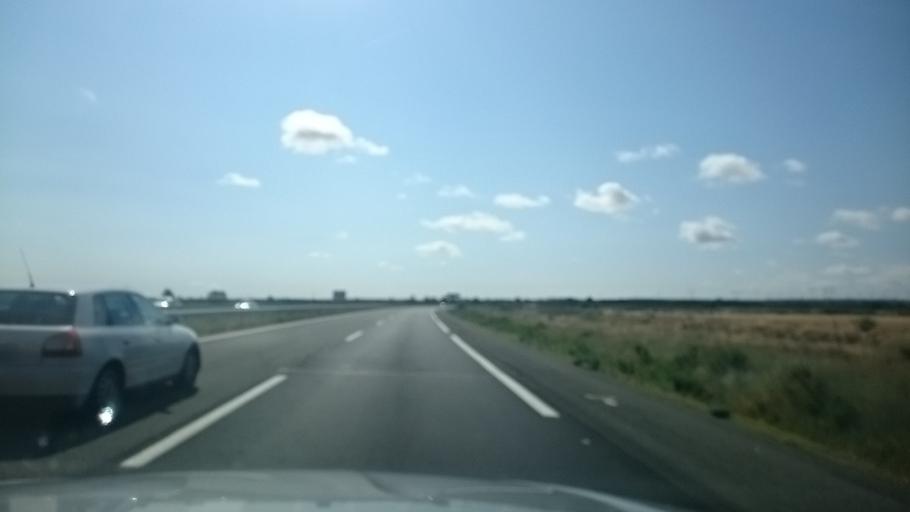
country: ES
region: Navarre
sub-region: Provincia de Navarra
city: Corella
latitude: 42.1309
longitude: -1.7627
